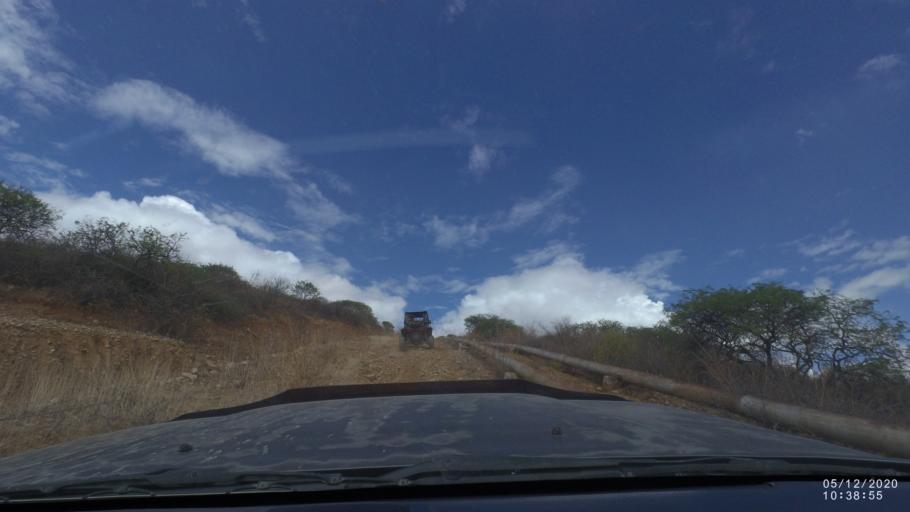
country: BO
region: Cochabamba
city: Sipe Sipe
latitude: -17.5457
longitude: -66.2829
